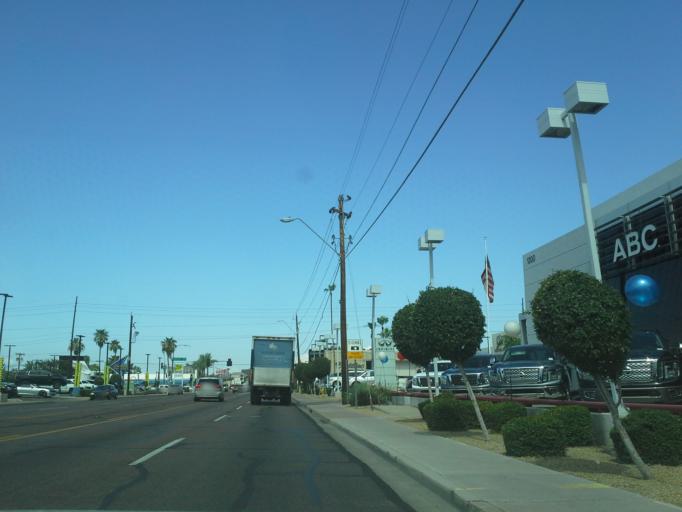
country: US
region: Arizona
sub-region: Maricopa County
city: Phoenix
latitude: 33.5093
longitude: -112.0546
